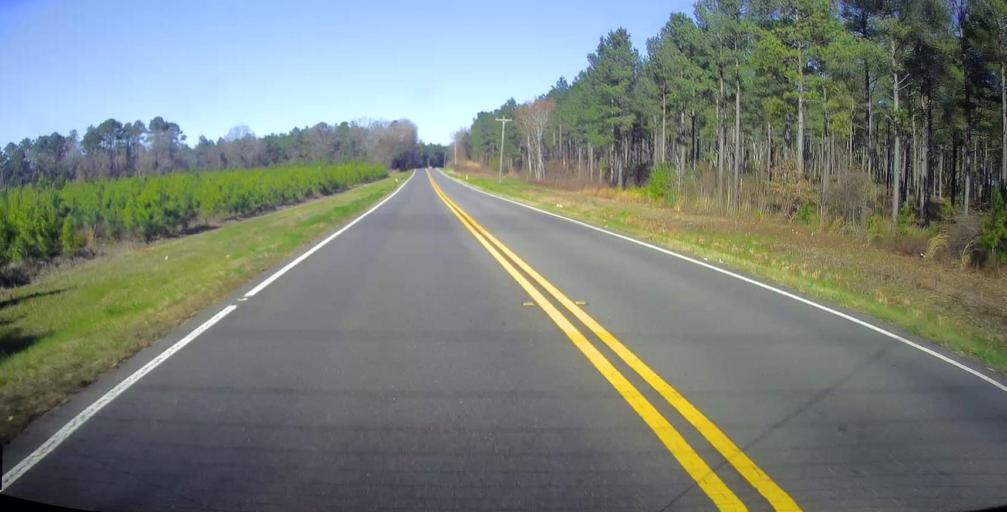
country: US
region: Georgia
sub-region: Macon County
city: Montezuma
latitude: 32.3465
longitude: -84.0192
